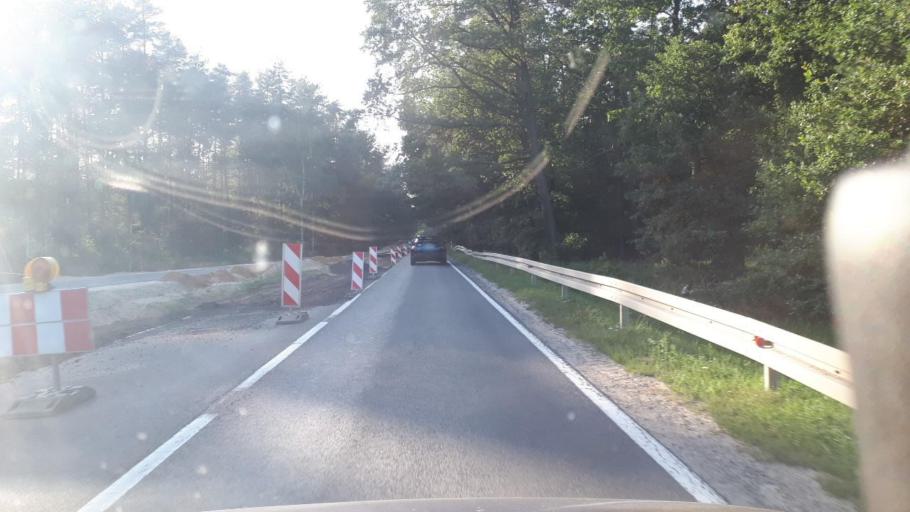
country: PL
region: Silesian Voivodeship
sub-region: Powiat lubliniecki
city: Sierakow Slaski
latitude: 50.8176
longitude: 18.5394
